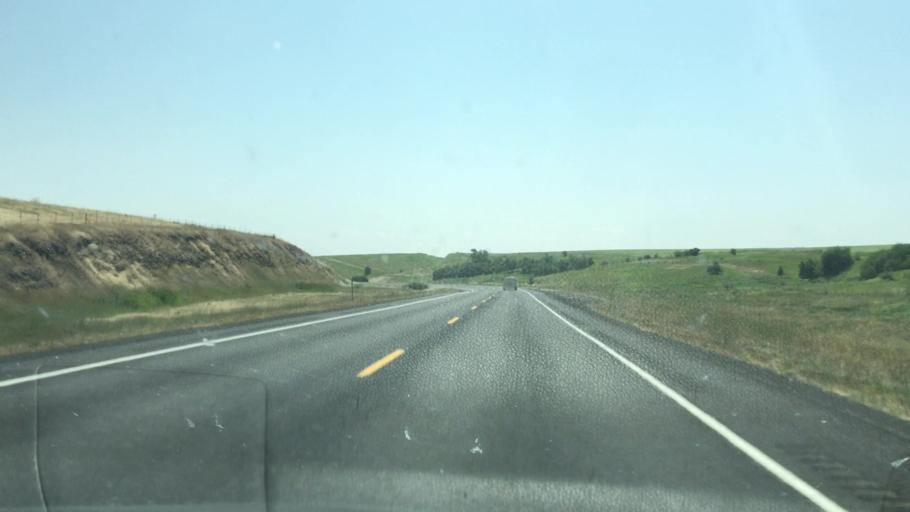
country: US
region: Idaho
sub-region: Lewis County
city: Nezperce
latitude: 46.2226
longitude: -116.4374
